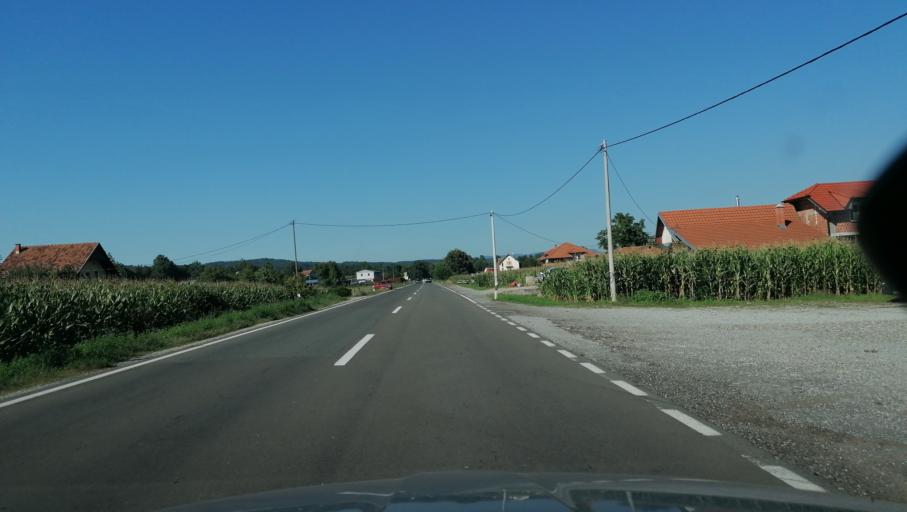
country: RS
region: Central Serbia
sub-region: Raski Okrug
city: Kraljevo
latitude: 43.6885
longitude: 20.5782
